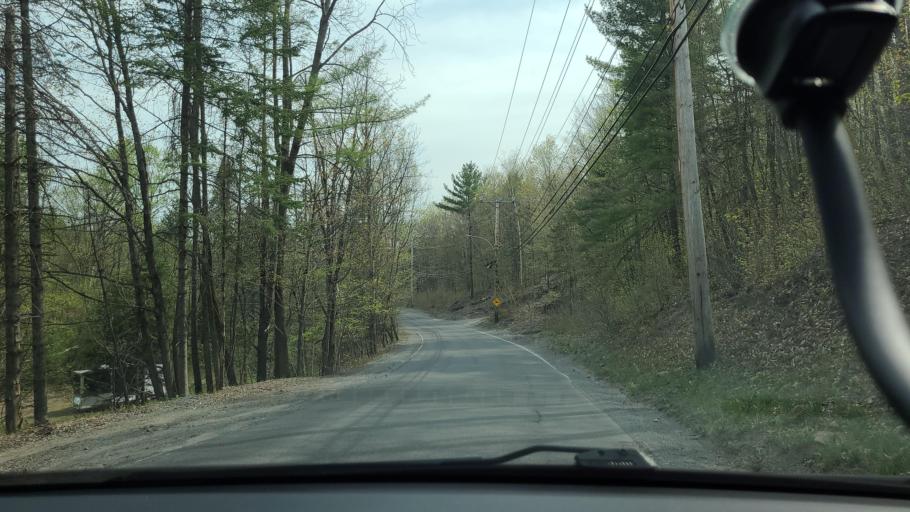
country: CA
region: Quebec
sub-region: Laurentides
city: Prevost
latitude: 45.8877
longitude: -74.0587
